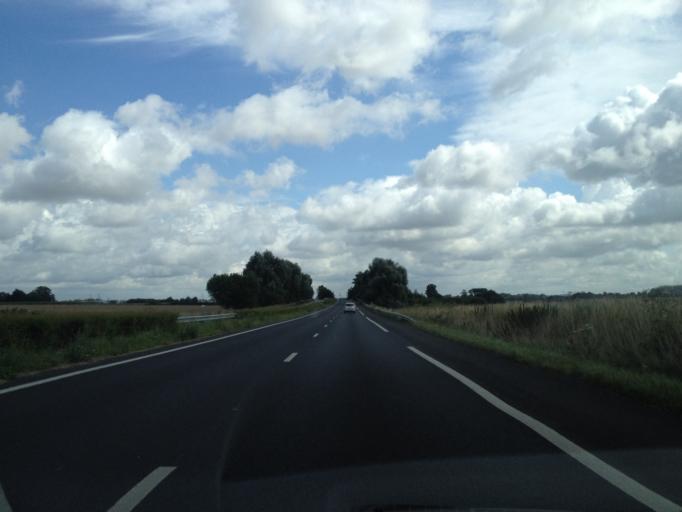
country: FR
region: Haute-Normandie
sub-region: Departement de la Seine-Maritime
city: Blainville-Crevon
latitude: 49.5578
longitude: 1.2626
